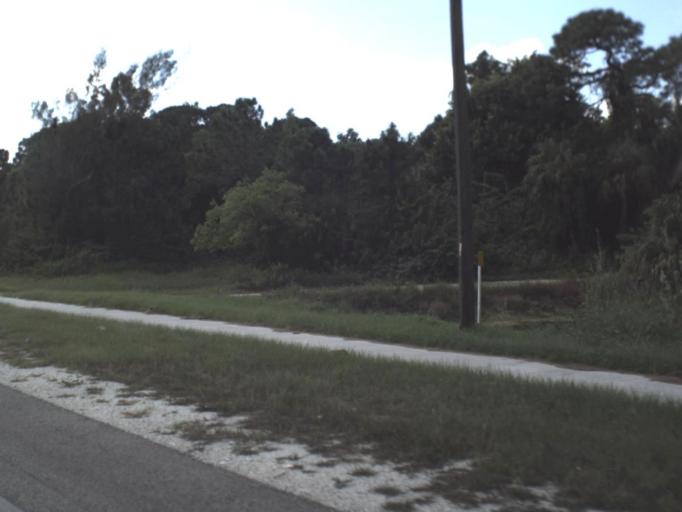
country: US
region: Florida
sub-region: Lee County
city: Palmona Park
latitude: 26.7146
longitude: -81.9032
